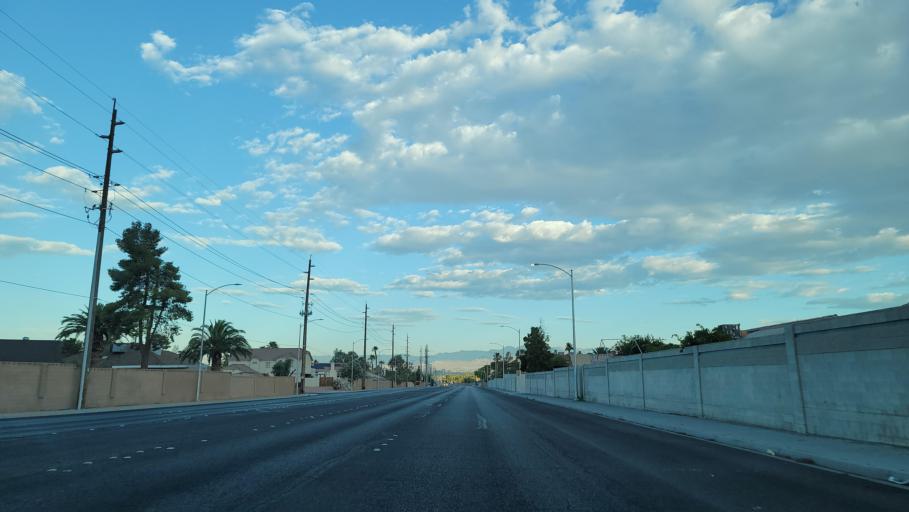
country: US
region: Nevada
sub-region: Clark County
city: Sunrise Manor
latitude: 36.1743
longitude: -115.0382
